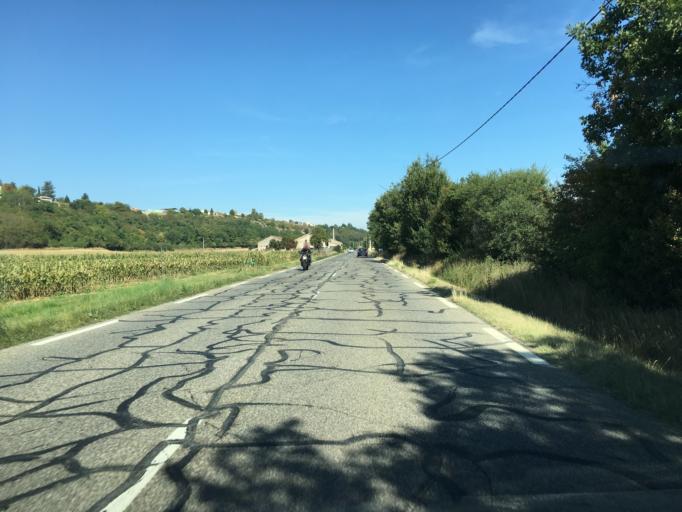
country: FR
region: Provence-Alpes-Cote d'Azur
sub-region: Departement des Alpes-de-Haute-Provence
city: Sisteron
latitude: 44.2404
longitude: 5.8958
